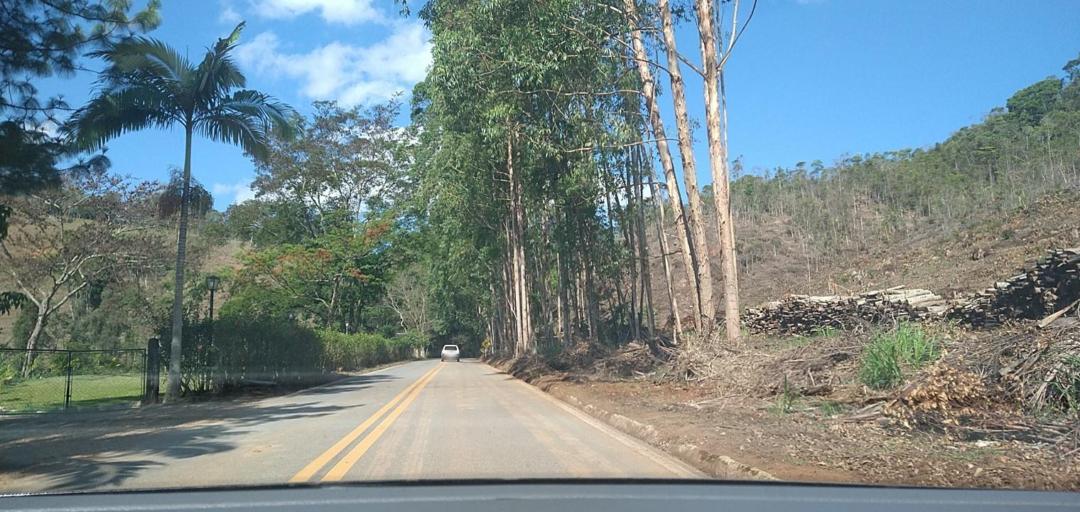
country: BR
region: Minas Gerais
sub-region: Alvinopolis
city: Alvinopolis
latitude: -20.0357
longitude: -43.0394
